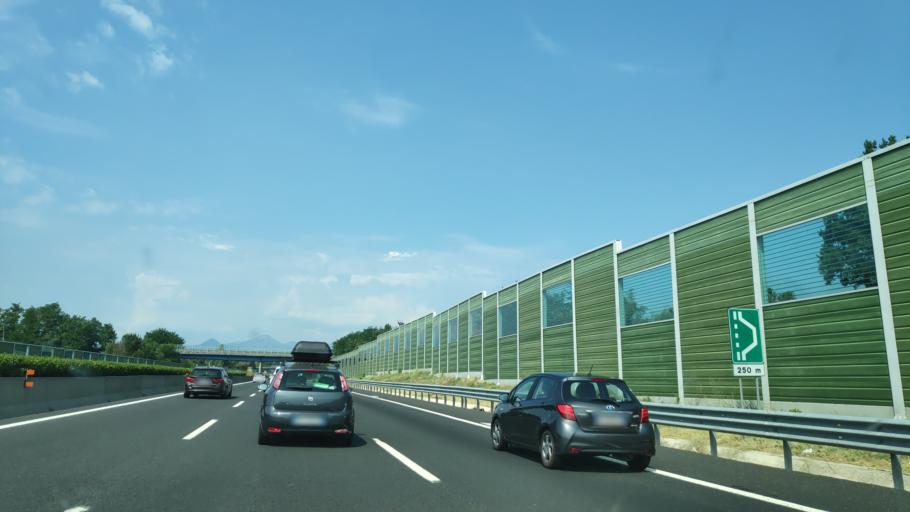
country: IT
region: Latium
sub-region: Provincia di Frosinone
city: Pofi
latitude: 41.5544
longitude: 13.4334
